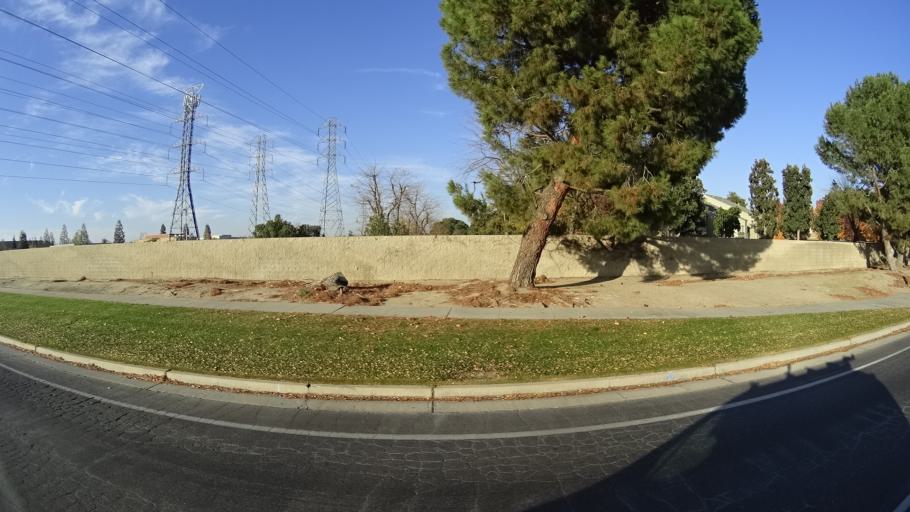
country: US
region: California
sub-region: Kern County
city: Greenacres
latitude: 35.3398
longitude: -119.0955
